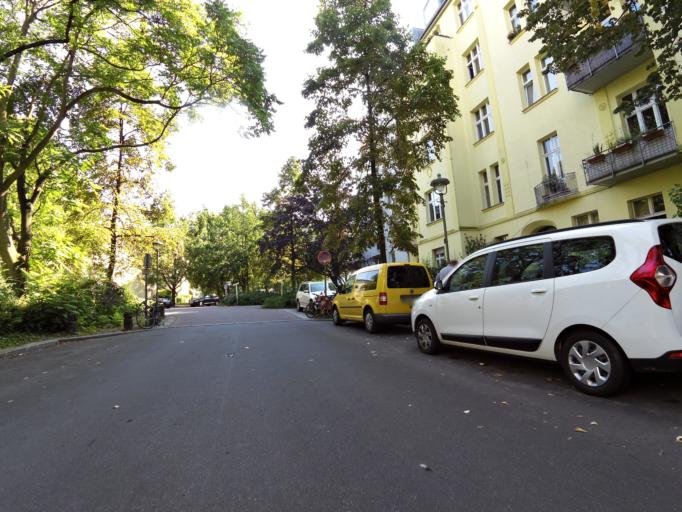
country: DE
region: Berlin
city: Berlin Schoeneberg
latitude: 52.4913
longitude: 13.3364
